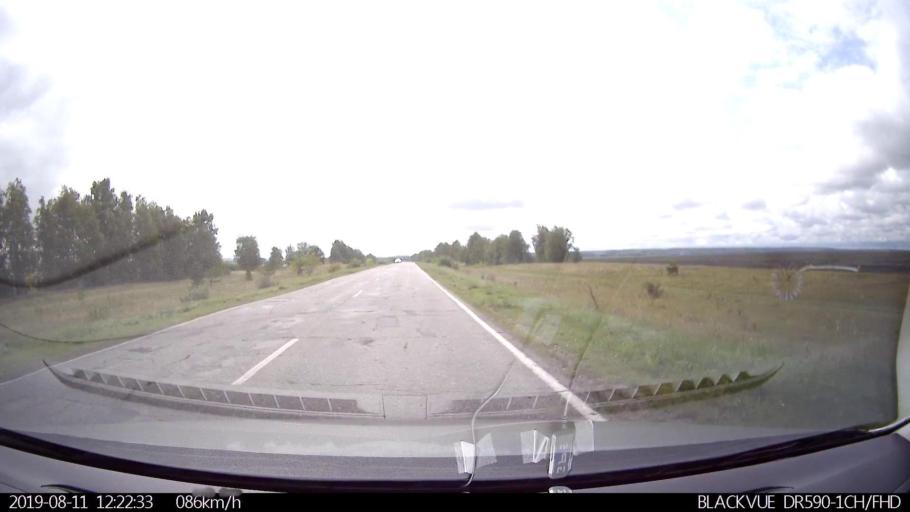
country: RU
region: Ulyanovsk
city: Ignatovka
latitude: 53.9064
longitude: 47.9533
